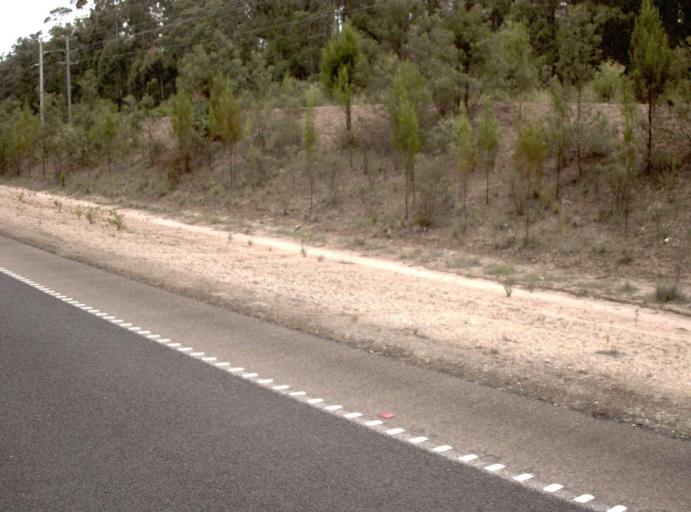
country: AU
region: Victoria
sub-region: East Gippsland
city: Lakes Entrance
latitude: -37.7072
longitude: 148.0689
